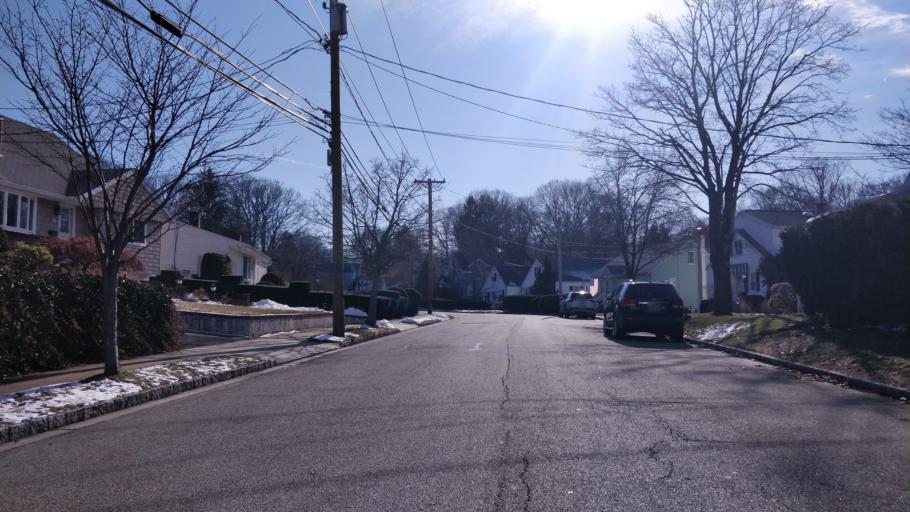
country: US
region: New York
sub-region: Nassau County
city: Oyster Bay
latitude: 40.8612
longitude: -73.5287
